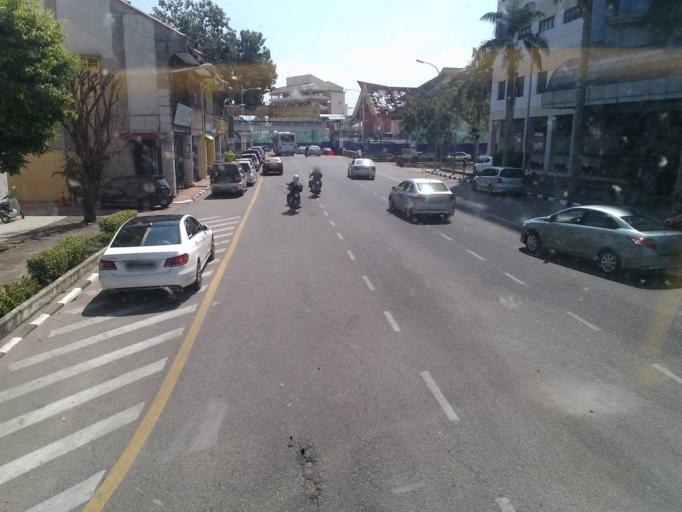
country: MY
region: Kedah
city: Alor Setar
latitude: 6.1179
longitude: 100.3658
